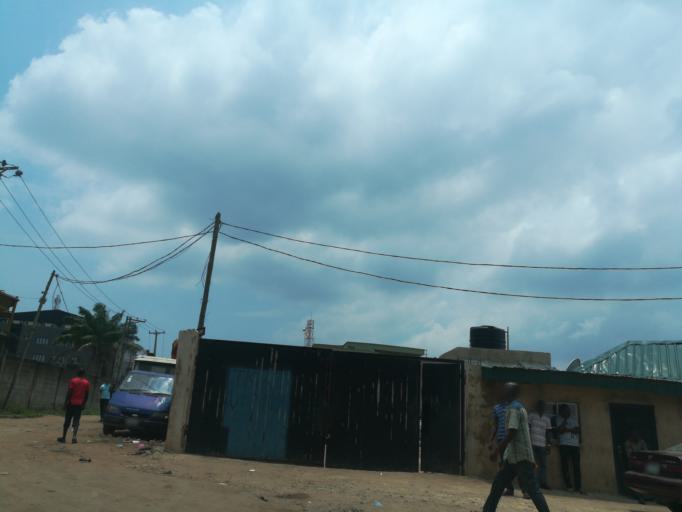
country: NG
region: Lagos
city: Ojota
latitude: 6.5931
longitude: 3.3682
